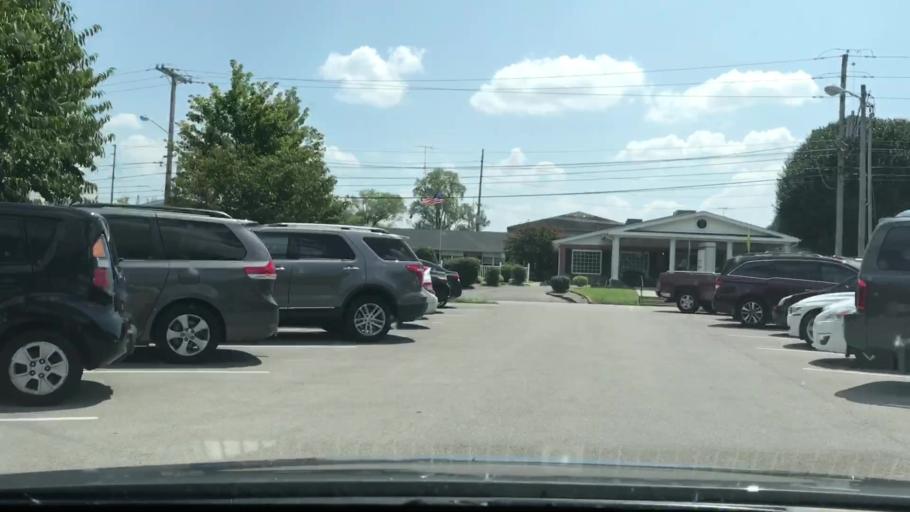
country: US
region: Kentucky
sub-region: Warren County
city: Bowling Green
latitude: 36.9931
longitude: -86.4335
